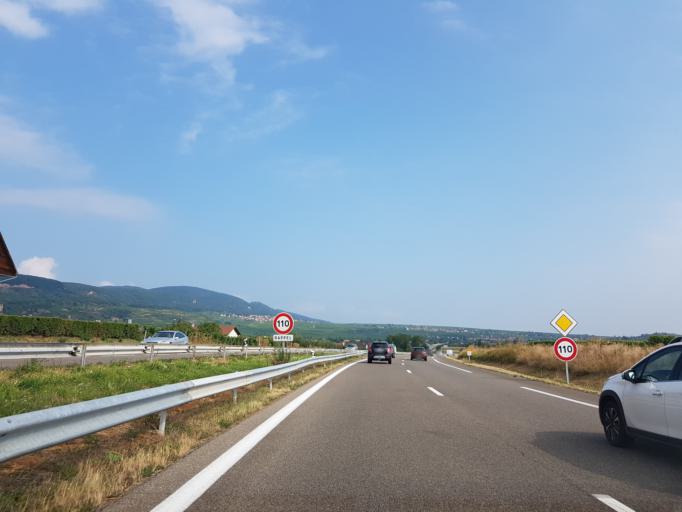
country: FR
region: Alsace
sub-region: Departement du Haut-Rhin
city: Pfaffenheim
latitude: 47.9850
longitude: 7.2930
